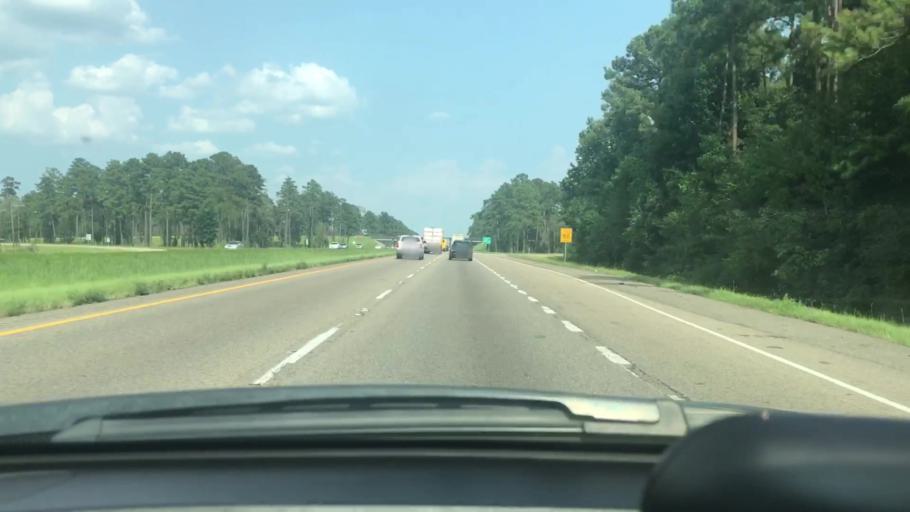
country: US
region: Louisiana
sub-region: Livingston Parish
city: Albany
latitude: 30.4746
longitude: -90.6480
